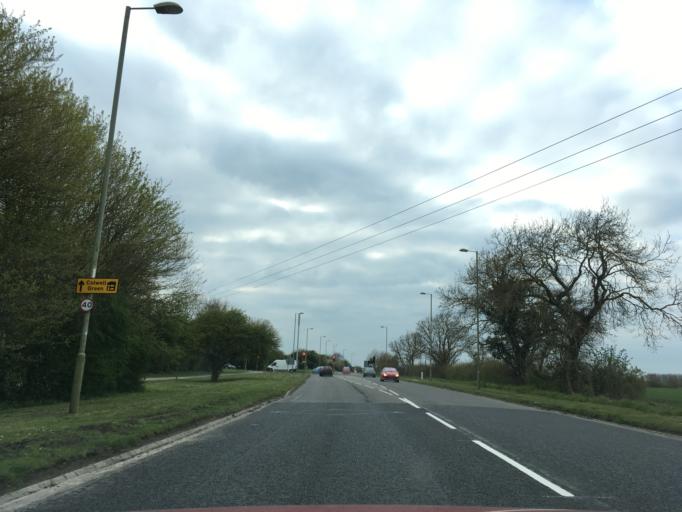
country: GB
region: England
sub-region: Oxfordshire
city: Witney
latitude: 51.7910
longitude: -1.5091
